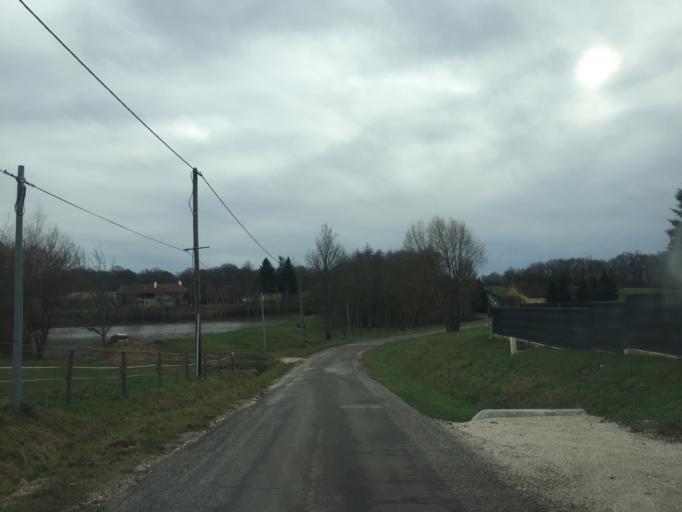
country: FR
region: Franche-Comte
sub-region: Departement du Jura
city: Chaussin
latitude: 46.9013
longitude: 5.4538
